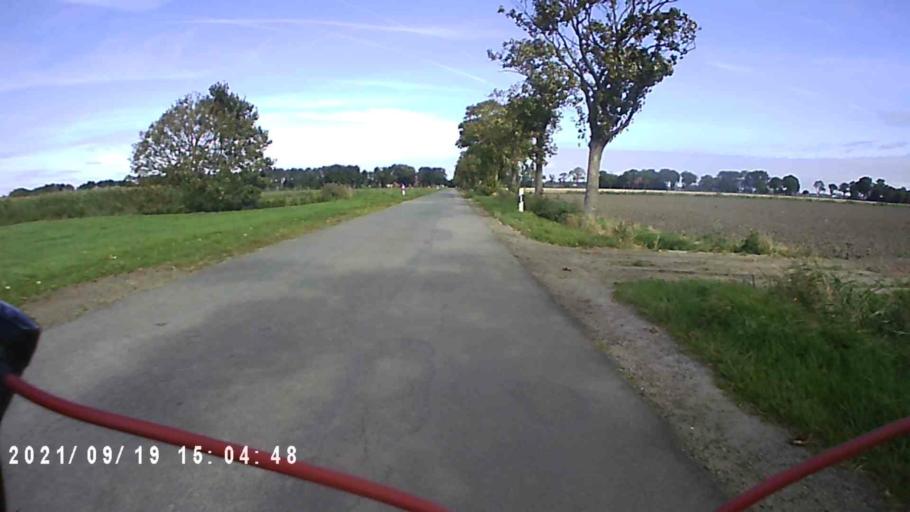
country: DE
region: Lower Saxony
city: Bunde
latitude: 53.1677
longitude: 7.2069
